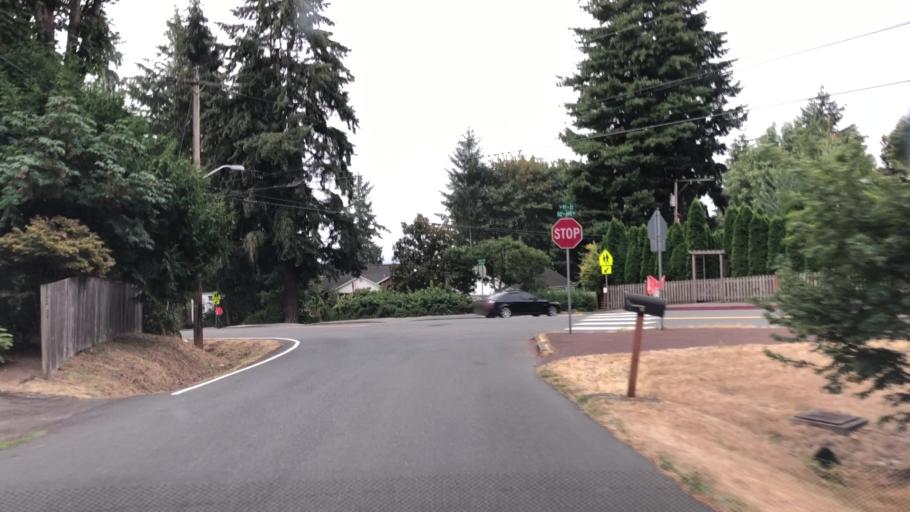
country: US
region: Washington
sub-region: King County
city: Kirkland
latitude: 47.6882
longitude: -122.1898
